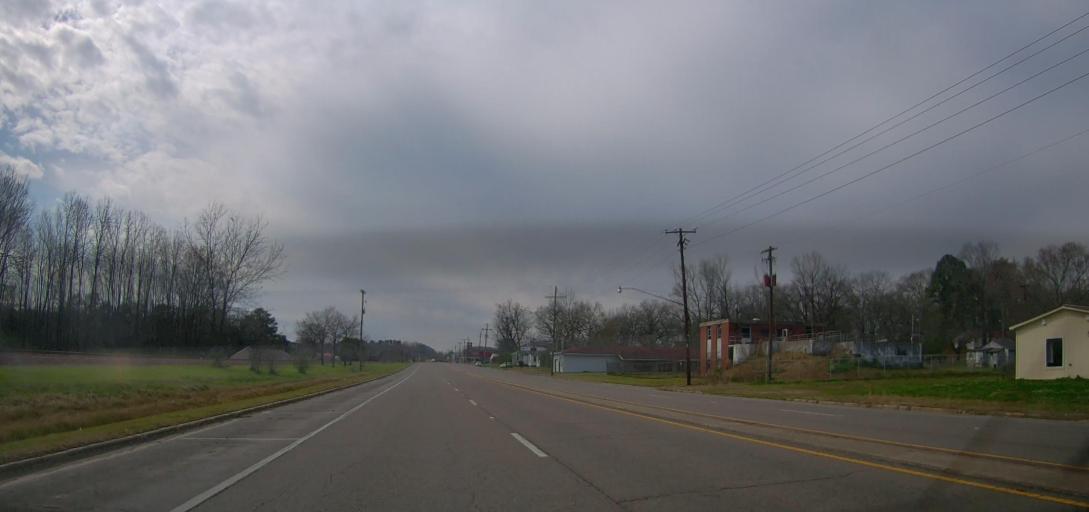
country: US
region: Alabama
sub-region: Walker County
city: Carbon Hill
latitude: 33.8868
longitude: -87.5243
